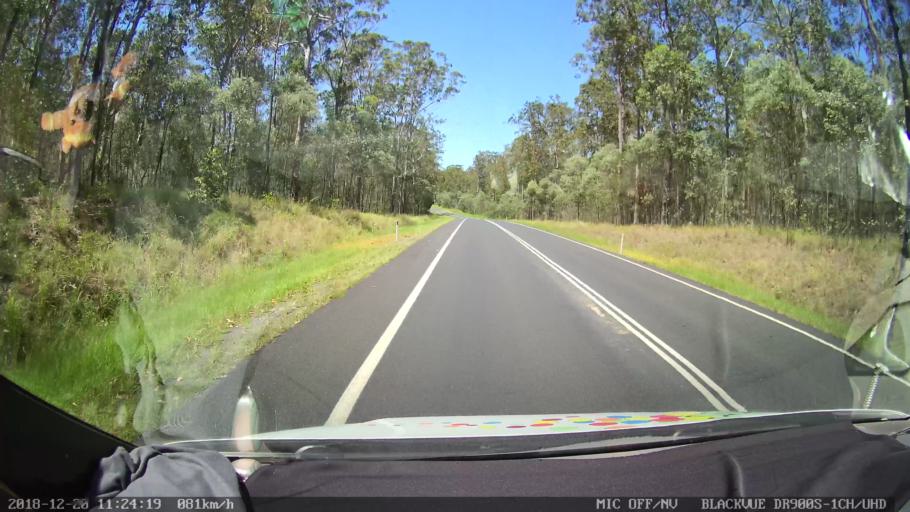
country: AU
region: New South Wales
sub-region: Richmond Valley
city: Casino
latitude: -29.0727
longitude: 153.0027
